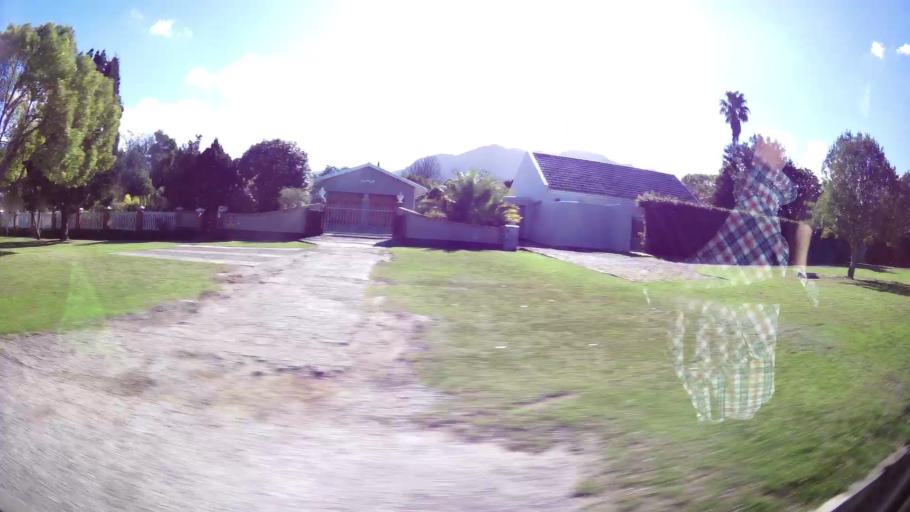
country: ZA
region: Western Cape
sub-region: Eden District Municipality
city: George
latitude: -33.9525
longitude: 22.4398
